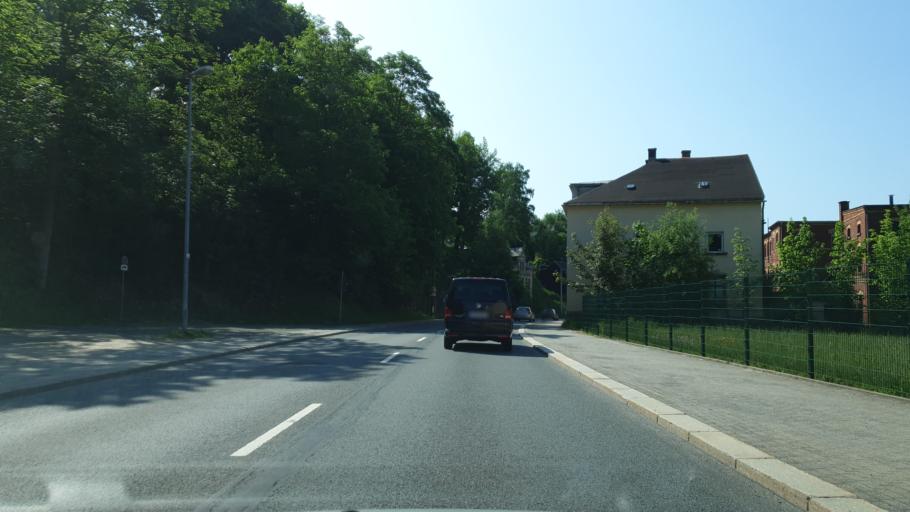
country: DE
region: Saxony
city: Klingenthal
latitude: 50.3623
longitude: 12.4696
